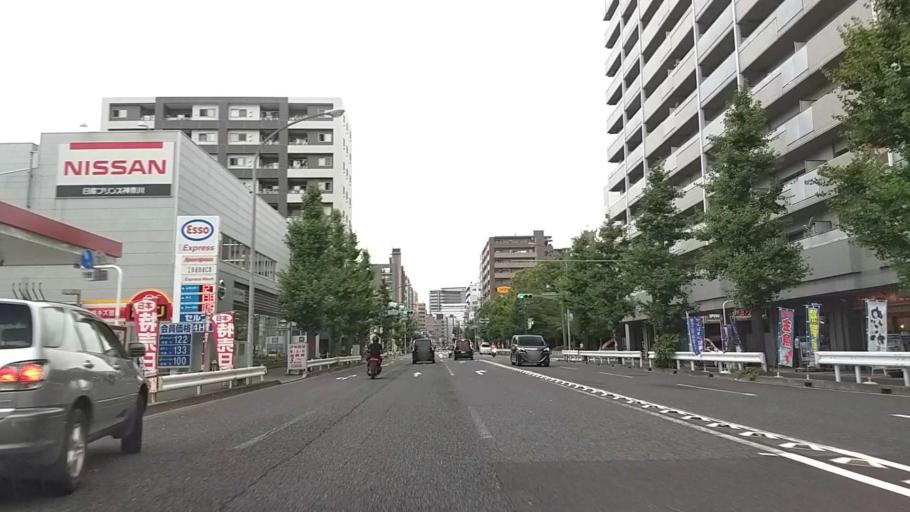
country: JP
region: Kanagawa
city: Yokohama
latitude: 35.4378
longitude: 139.6345
